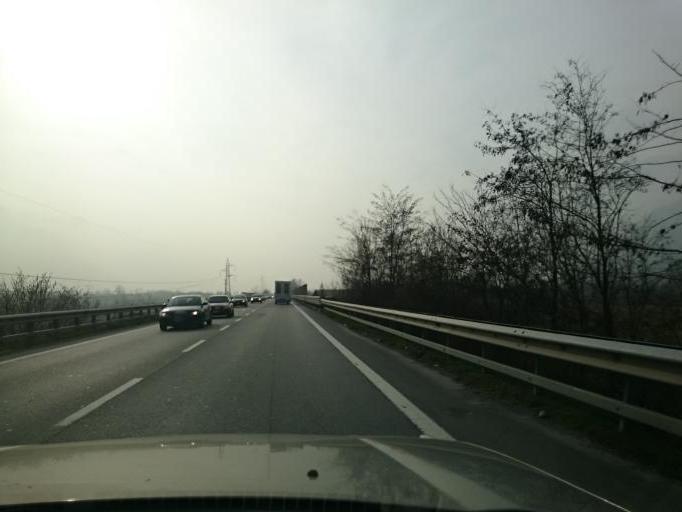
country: IT
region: Lombardy
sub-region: Provincia di Brescia
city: Artogne
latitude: 45.8577
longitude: 10.1504
